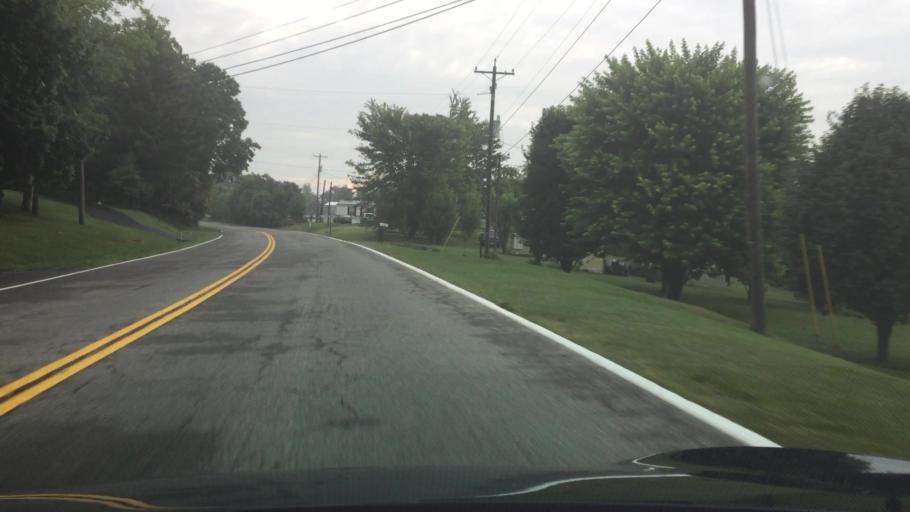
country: US
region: Virginia
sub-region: Pulaski County
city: Pulaski
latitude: 36.9581
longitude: -80.8614
